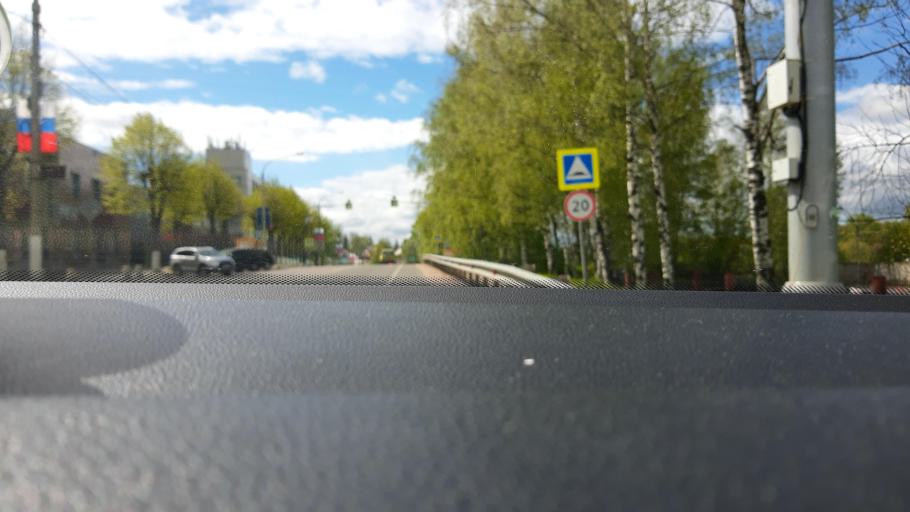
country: RU
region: Moskovskaya
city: Dmitrov
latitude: 56.3347
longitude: 37.5104
